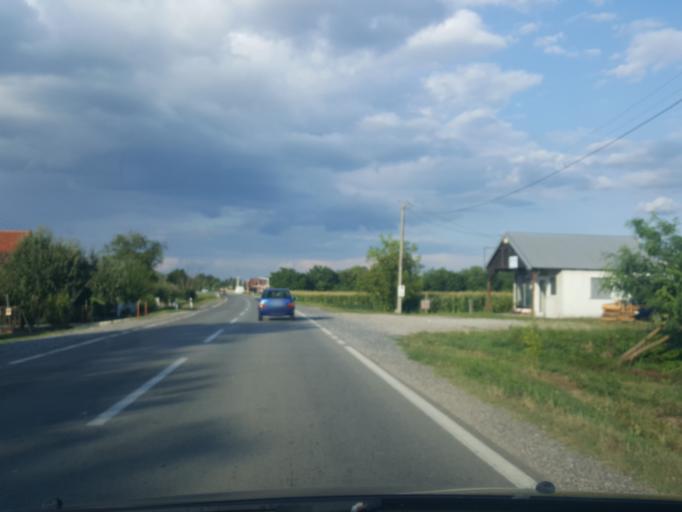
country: RS
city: Lesnica
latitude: 44.6456
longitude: 19.2911
